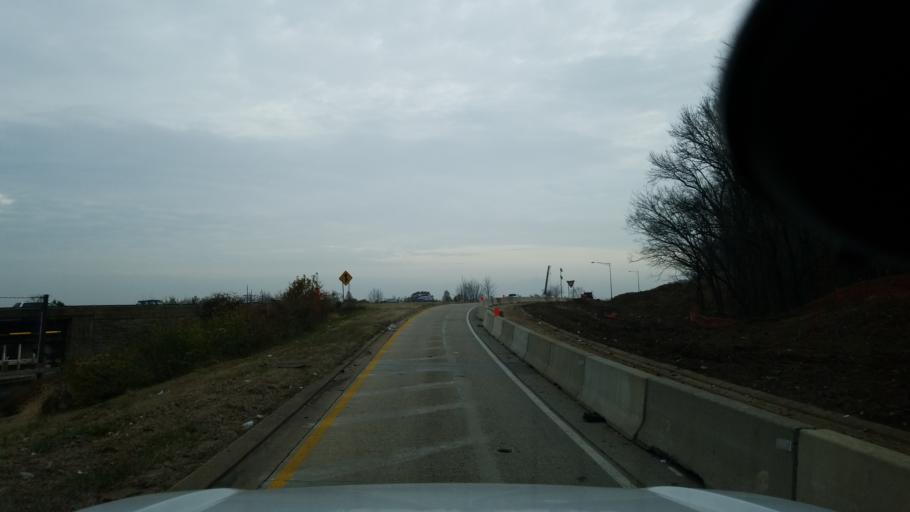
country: US
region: Maryland
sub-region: Prince George's County
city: Glassmanor
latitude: 38.8380
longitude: -77.0084
